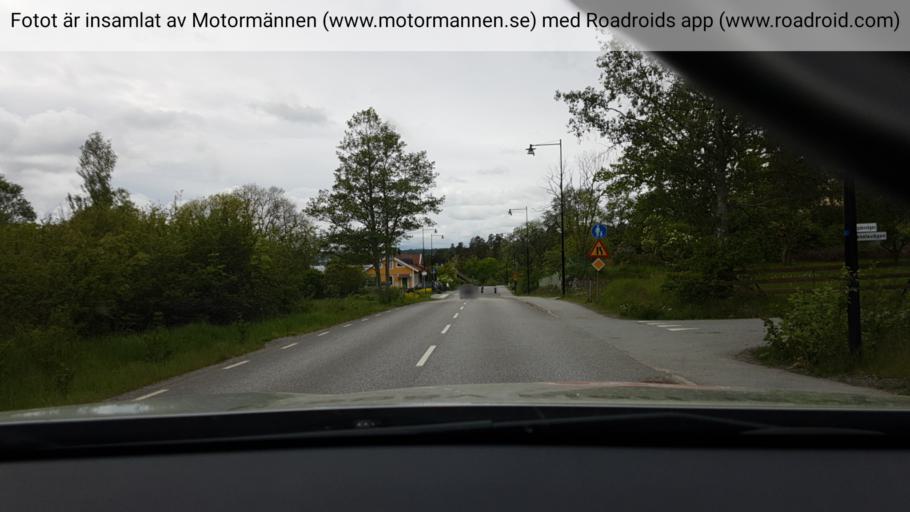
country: SE
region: Stockholm
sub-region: Nacka Kommun
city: Saltsjobaden
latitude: 59.2646
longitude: 18.3511
